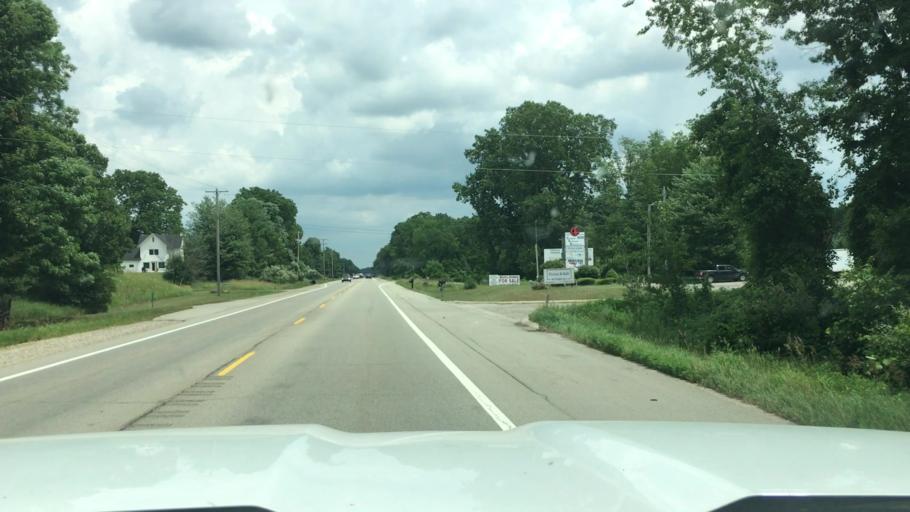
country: US
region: Michigan
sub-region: Montcalm County
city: Greenville
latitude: 43.1763
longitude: -85.3811
